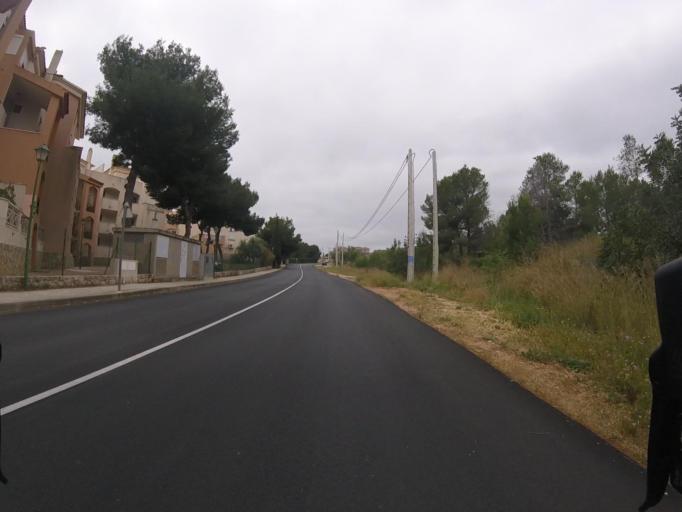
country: ES
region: Valencia
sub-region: Provincia de Castello
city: Peniscola
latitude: 40.3450
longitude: 0.3861
